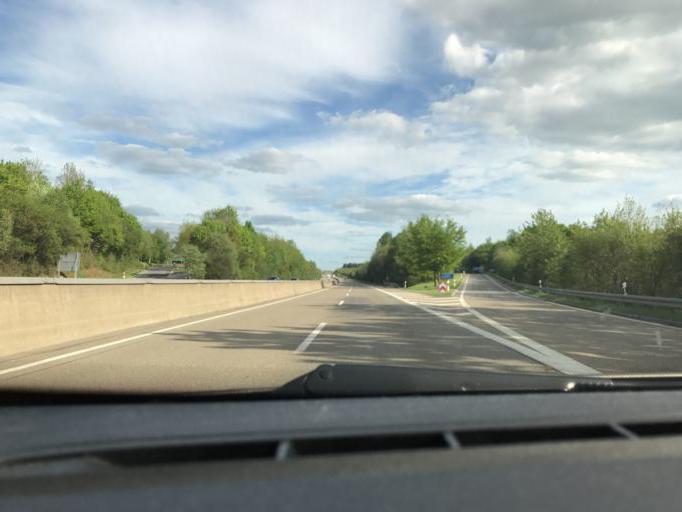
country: DE
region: North Rhine-Westphalia
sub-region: Regierungsbezirk Koln
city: Nettersheim
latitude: 50.4911
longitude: 6.6722
